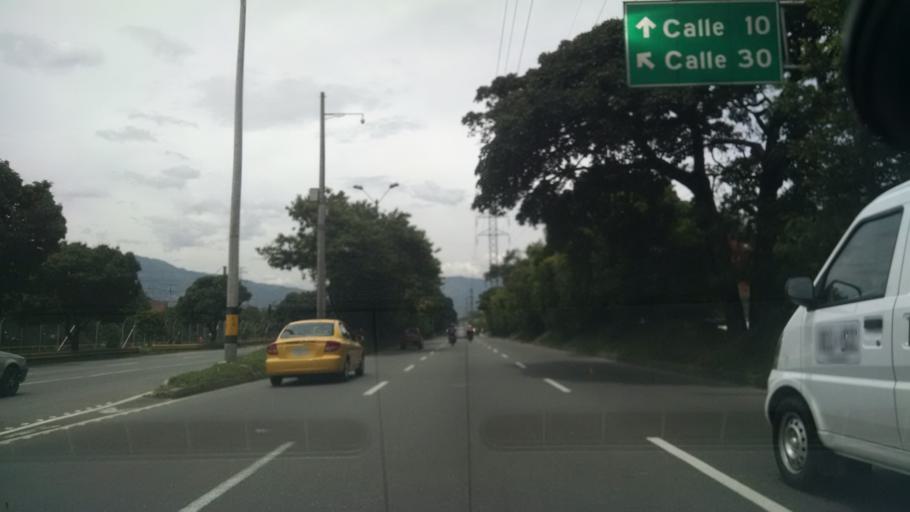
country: CO
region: Antioquia
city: Itagui
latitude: 6.2085
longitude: -75.5783
